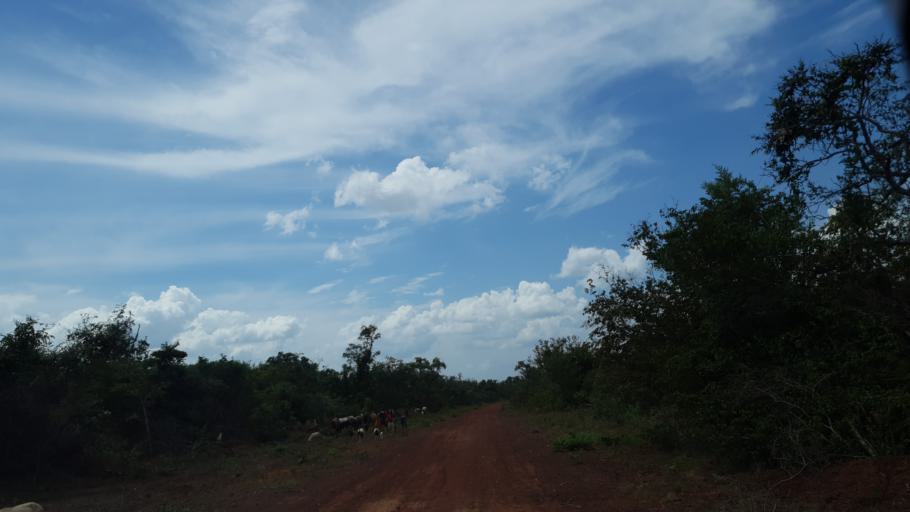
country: ML
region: Sikasso
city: Sikasso
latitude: 11.6863
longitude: -6.2129
